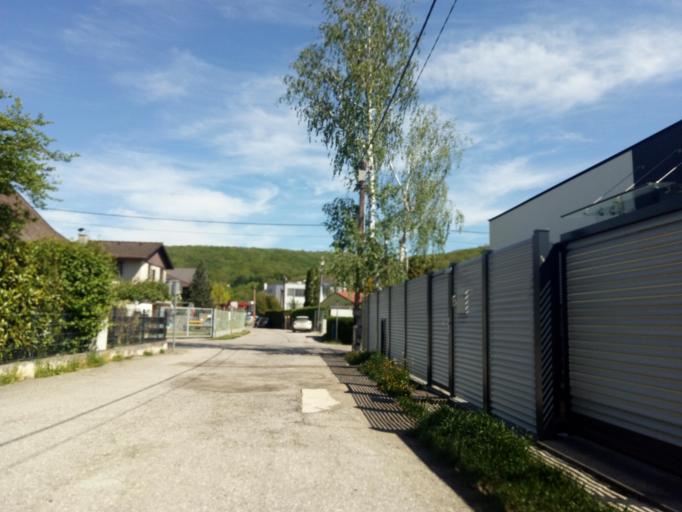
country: AT
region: Lower Austria
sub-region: Politischer Bezirk Modling
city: Kaltenleutgeben
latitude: 48.1365
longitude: 16.2042
